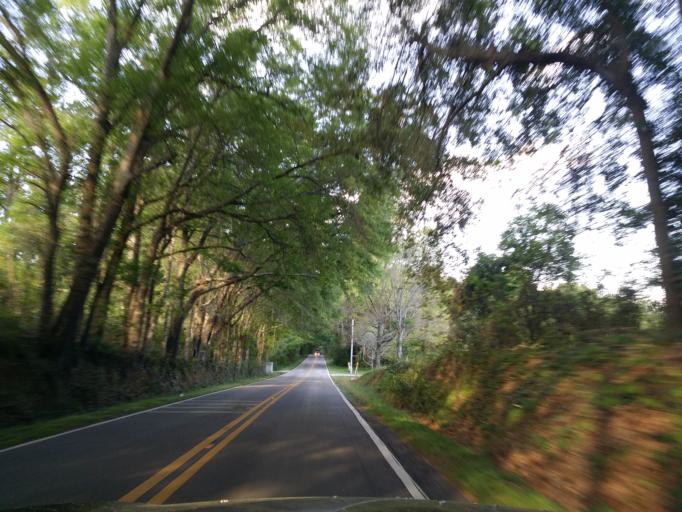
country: US
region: Florida
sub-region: Leon County
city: Tallahassee
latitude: 30.5187
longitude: -84.1272
